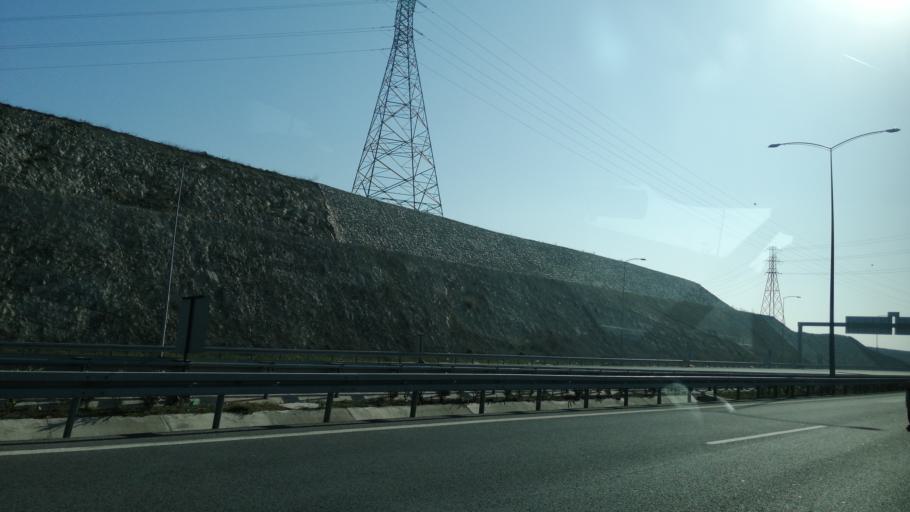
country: TR
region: Kocaeli
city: Tavsanli
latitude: 40.7937
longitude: 29.5113
